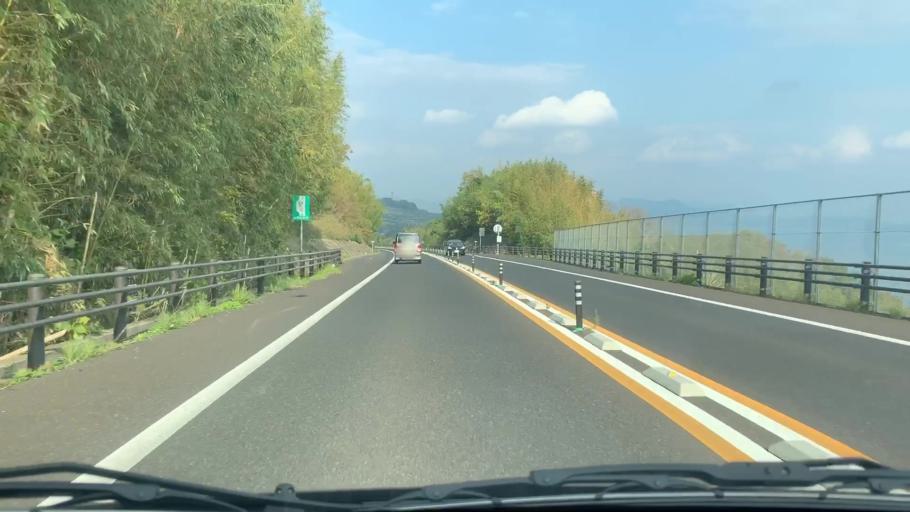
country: JP
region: Nagasaki
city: Sasebo
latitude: 33.0336
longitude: 129.7418
